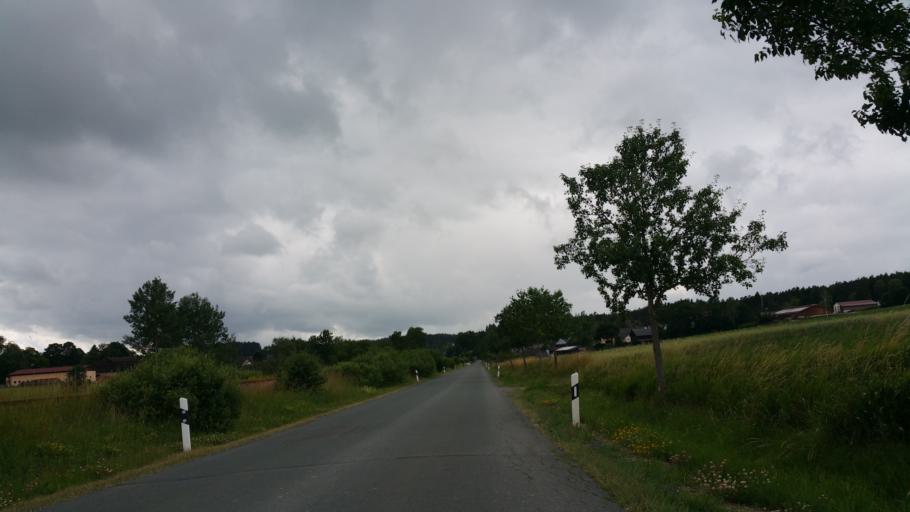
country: DE
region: Bavaria
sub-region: Upper Franconia
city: Rehau
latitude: 50.2537
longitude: 11.9975
